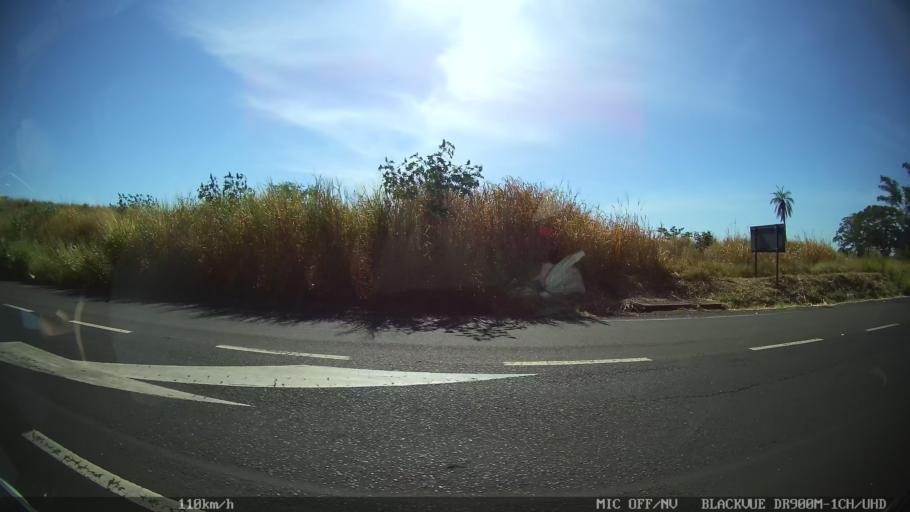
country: BR
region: Sao Paulo
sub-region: Barretos
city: Barretos
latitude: -20.6094
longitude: -48.7493
